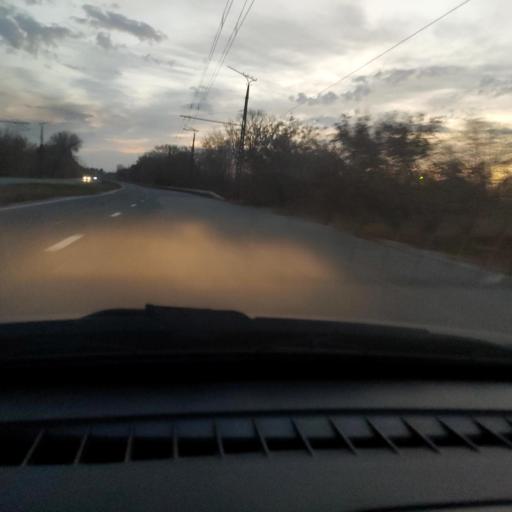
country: RU
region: Samara
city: Zhigulevsk
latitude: 53.5395
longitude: 49.5672
